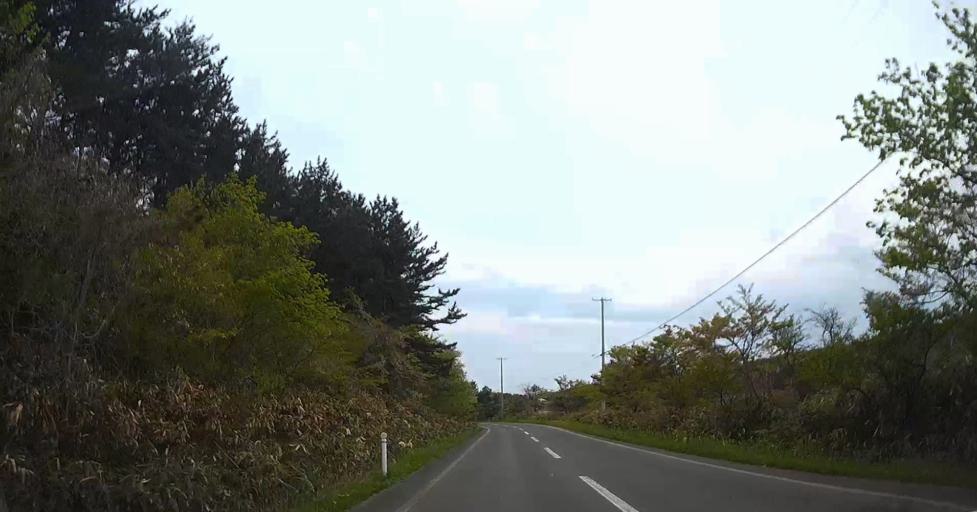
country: JP
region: Aomori
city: Shimokizukuri
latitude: 40.9379
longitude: 140.3193
